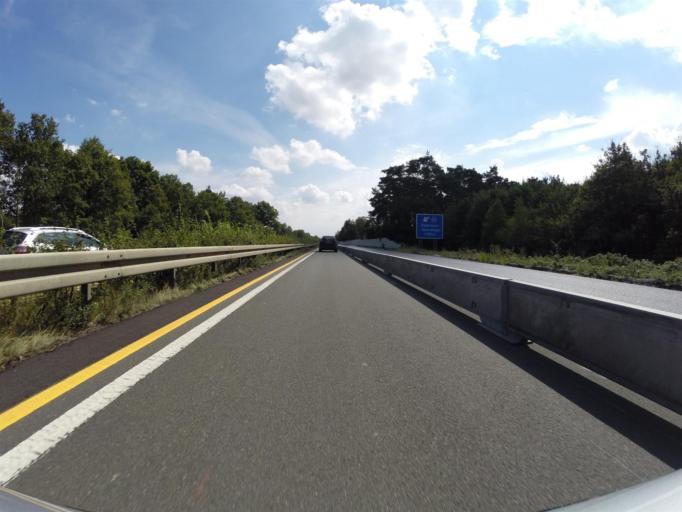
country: DE
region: North Rhine-Westphalia
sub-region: Regierungsbezirk Detmold
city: Hovelhof
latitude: 51.7903
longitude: 8.7035
